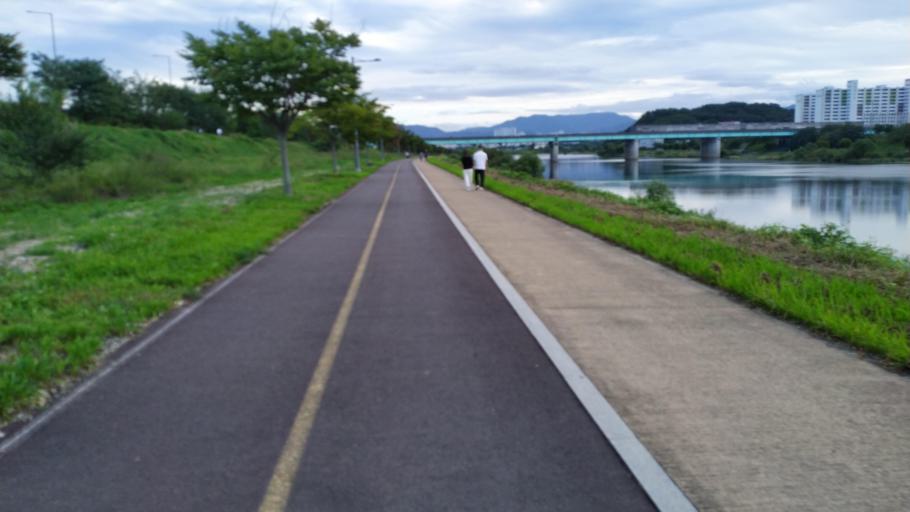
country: KR
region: Daegu
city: Daegu
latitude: 35.9213
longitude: 128.6328
